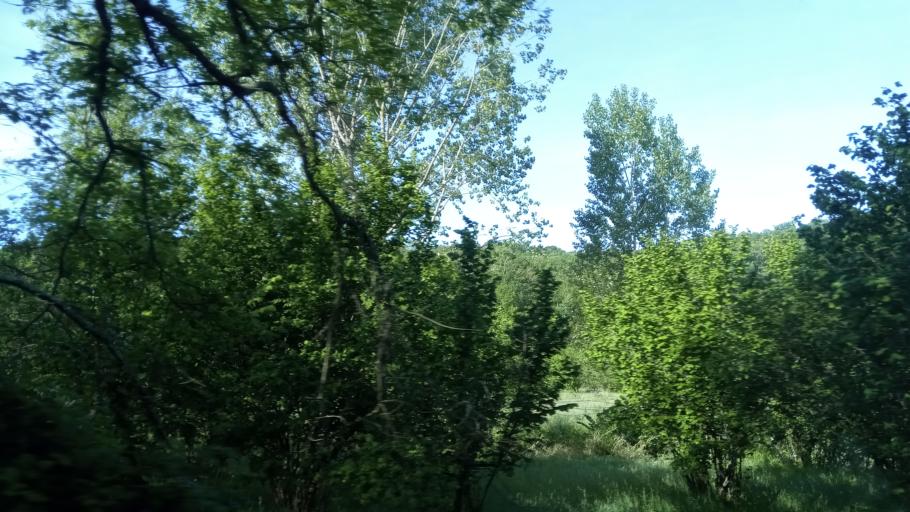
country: IT
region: Latium
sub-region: Provincia di Latina
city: Spigno Saturnia Inferiore
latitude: 41.2830
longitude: 13.7635
